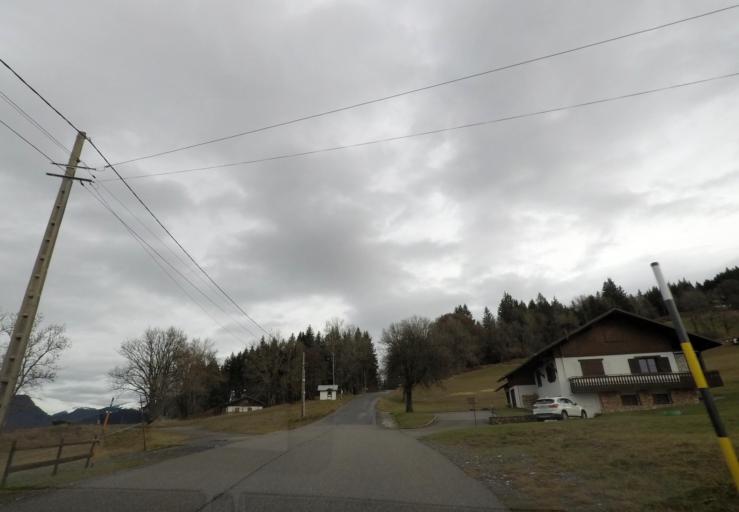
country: FR
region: Rhone-Alpes
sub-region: Departement de la Haute-Savoie
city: Chatillon-sur-Cluses
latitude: 46.0807
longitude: 6.6108
